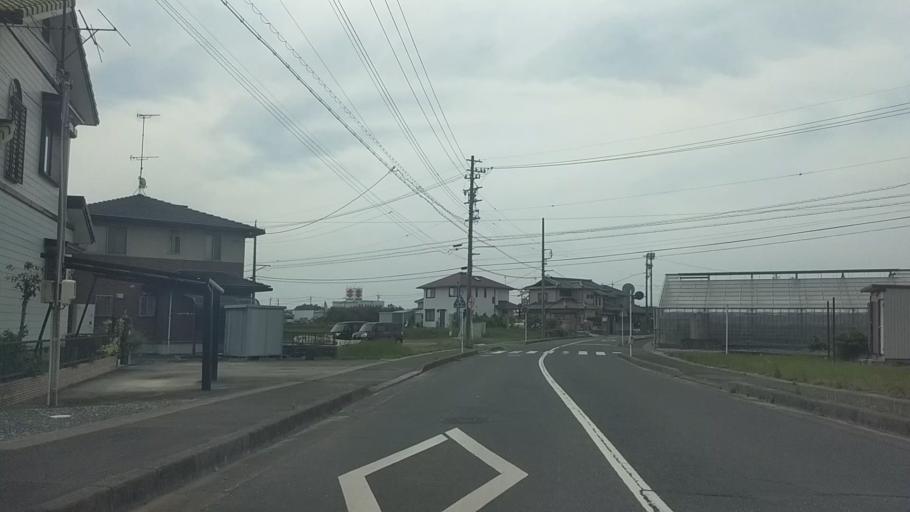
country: JP
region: Shizuoka
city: Kosai-shi
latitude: 34.7303
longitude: 137.5252
